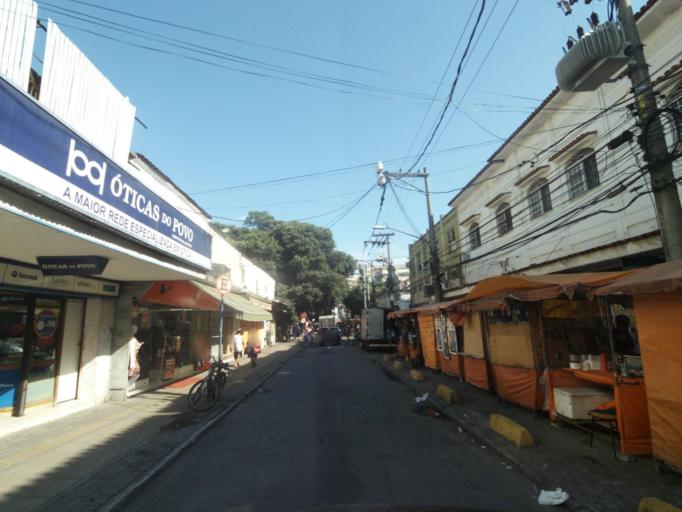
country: BR
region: Rio de Janeiro
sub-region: Niteroi
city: Niteroi
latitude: -22.8909
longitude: -43.1224
